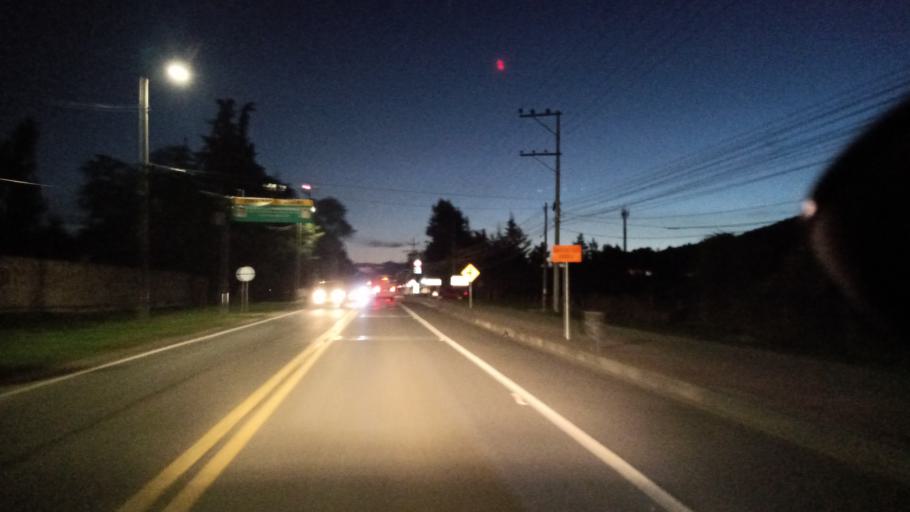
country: CO
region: Cundinamarca
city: Cota
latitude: 4.8004
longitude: -74.1098
